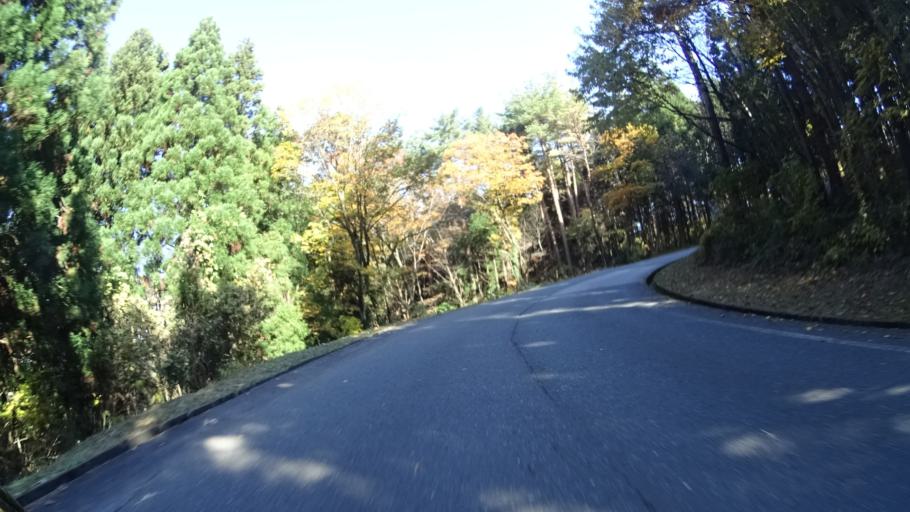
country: JP
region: Niigata
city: Itoigawa
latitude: 37.0210
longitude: 137.8689
